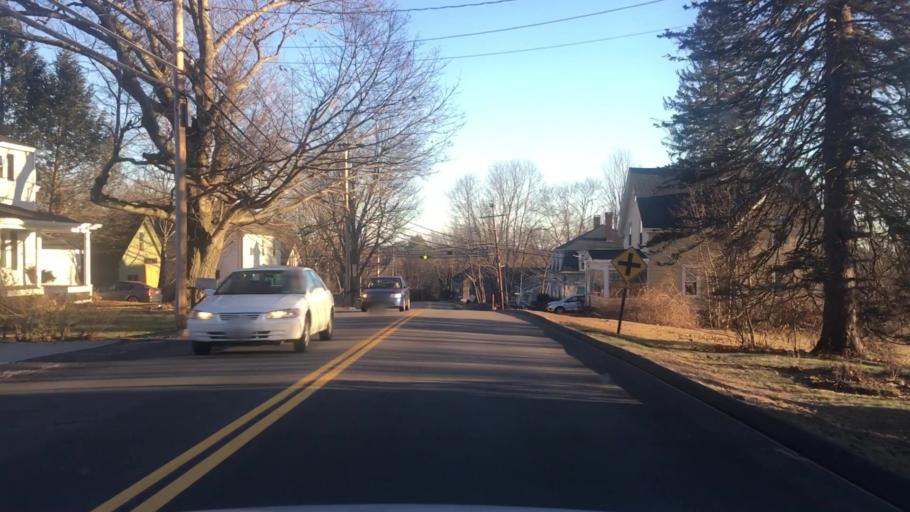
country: US
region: Maine
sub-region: York County
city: South Eliot
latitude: 43.1116
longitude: -70.7759
